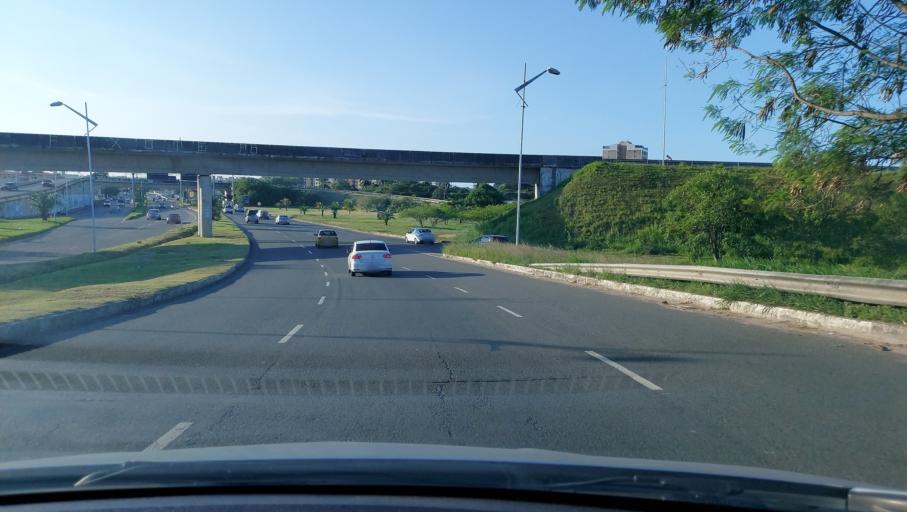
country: BR
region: Bahia
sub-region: Lauro De Freitas
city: Lauro de Freitas
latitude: -12.9088
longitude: -38.3491
